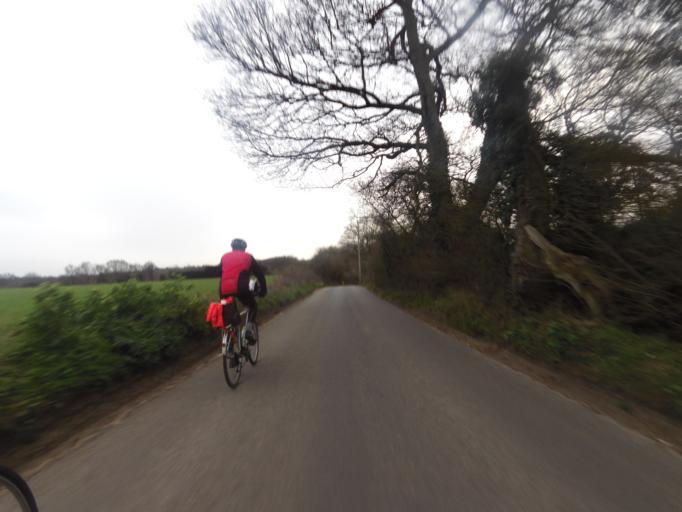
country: GB
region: England
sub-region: Suffolk
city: Kesgrave
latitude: 52.0882
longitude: 1.2307
